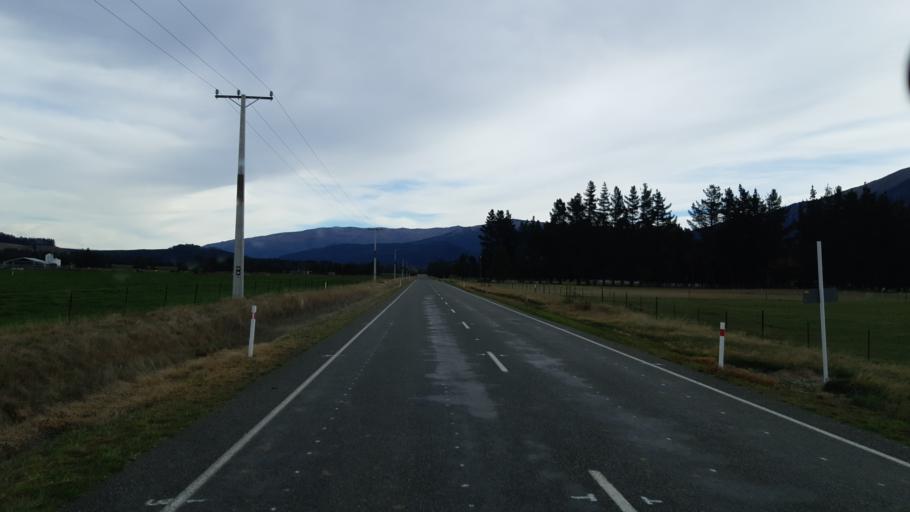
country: NZ
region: Tasman
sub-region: Tasman District
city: Brightwater
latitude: -41.6532
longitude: 173.2745
